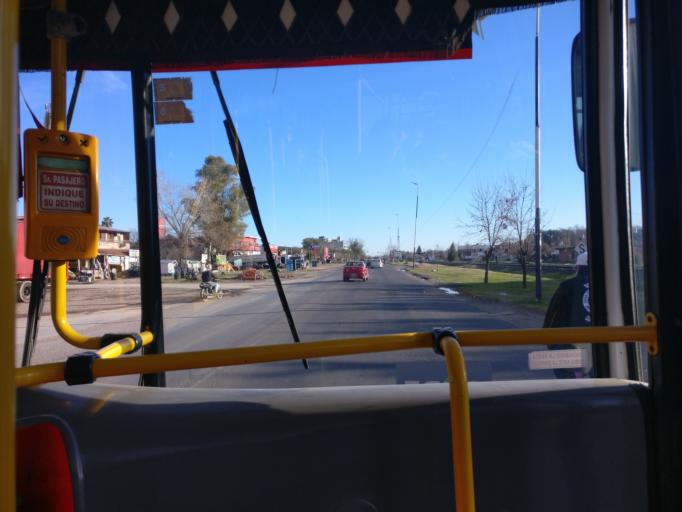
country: AR
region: Buenos Aires
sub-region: Partido de Ezeiza
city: Ezeiza
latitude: -34.8780
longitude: -58.5529
